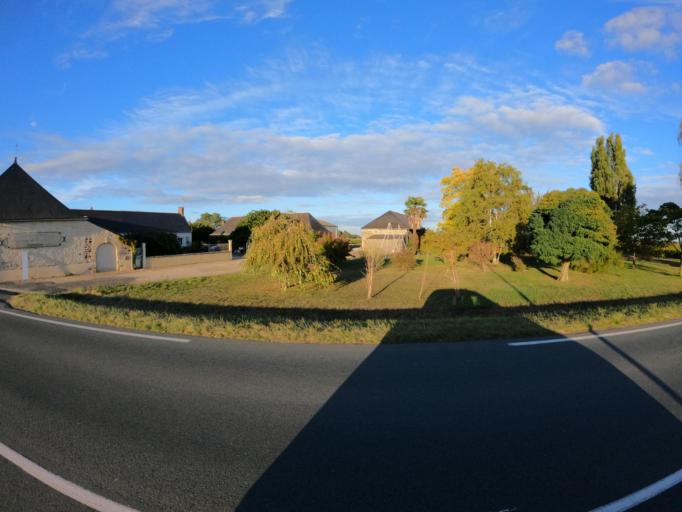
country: FR
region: Pays de la Loire
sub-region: Departement de Maine-et-Loire
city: Brissac-Quince
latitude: 47.3247
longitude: -0.4152
